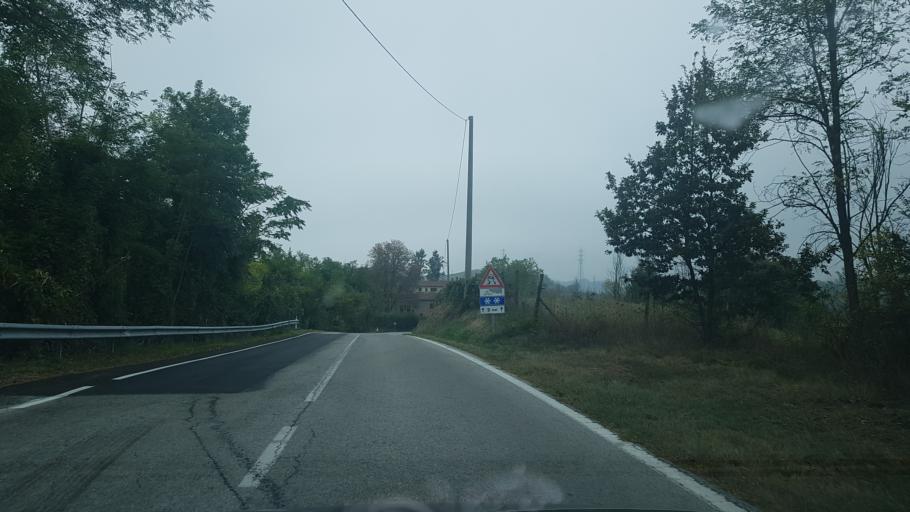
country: IT
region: Piedmont
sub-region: Provincia di Cuneo
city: Sale delle Langhe
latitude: 44.4047
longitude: 8.1111
